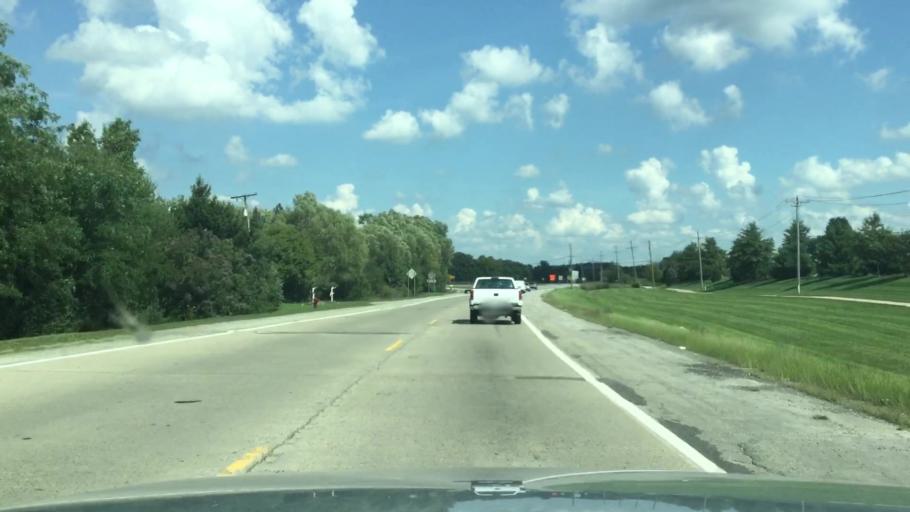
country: US
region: Michigan
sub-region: Washtenaw County
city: Saline
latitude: 42.1935
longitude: -83.7175
